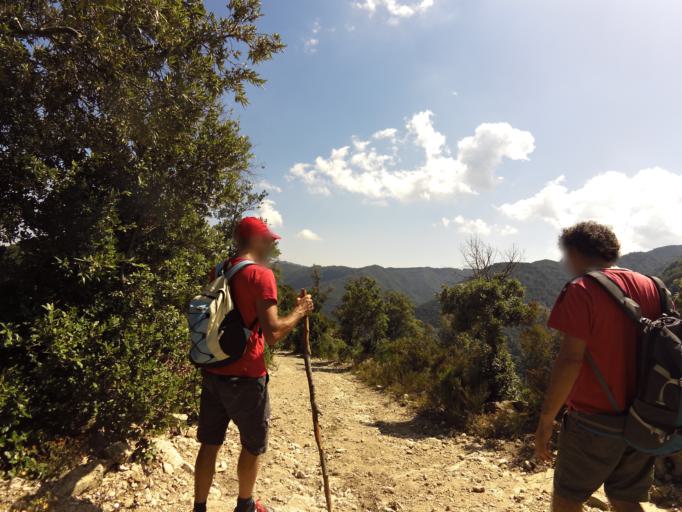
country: IT
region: Calabria
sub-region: Provincia di Reggio Calabria
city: Bivongi
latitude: 38.5050
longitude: 16.3983
